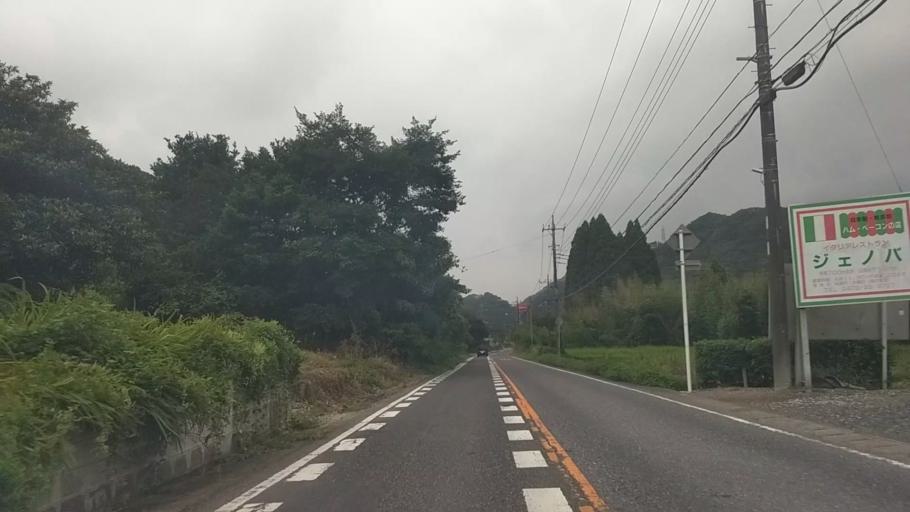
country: JP
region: Chiba
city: Tateyama
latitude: 35.1429
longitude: 139.8797
